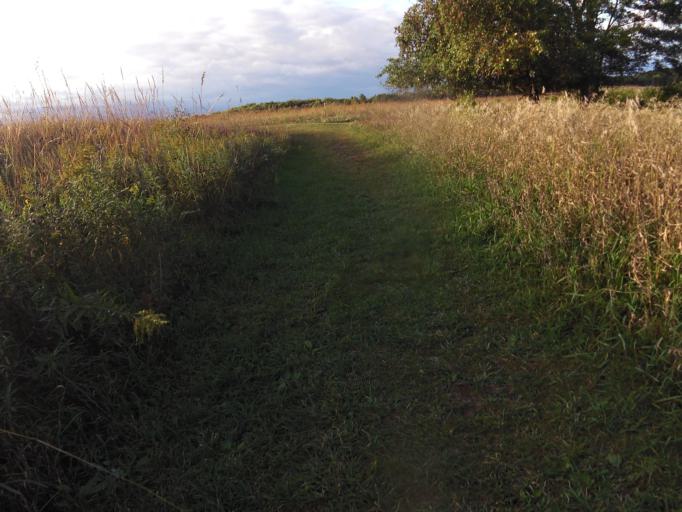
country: US
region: Minnesota
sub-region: Washington County
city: Lake Saint Croix Beach
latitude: 44.9341
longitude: -92.7882
